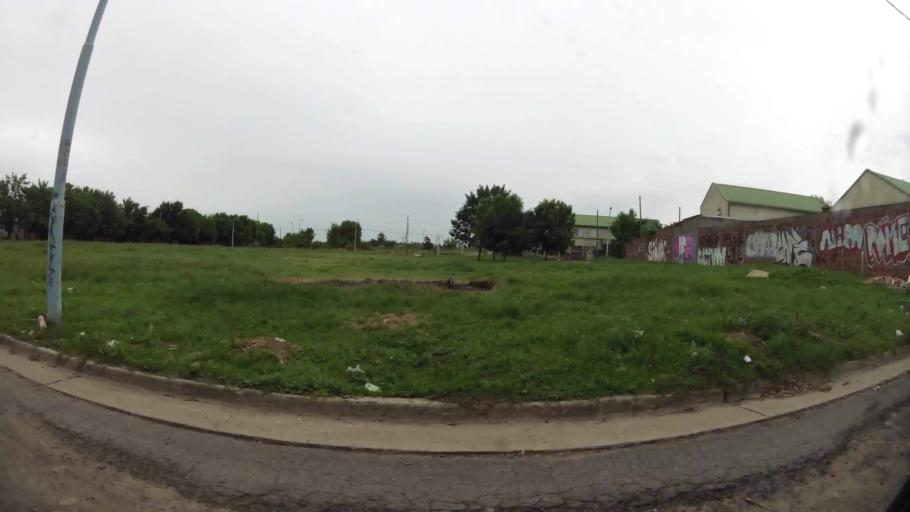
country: AR
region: Buenos Aires
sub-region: Partido de Campana
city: Campana
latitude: -34.1990
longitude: -58.9421
